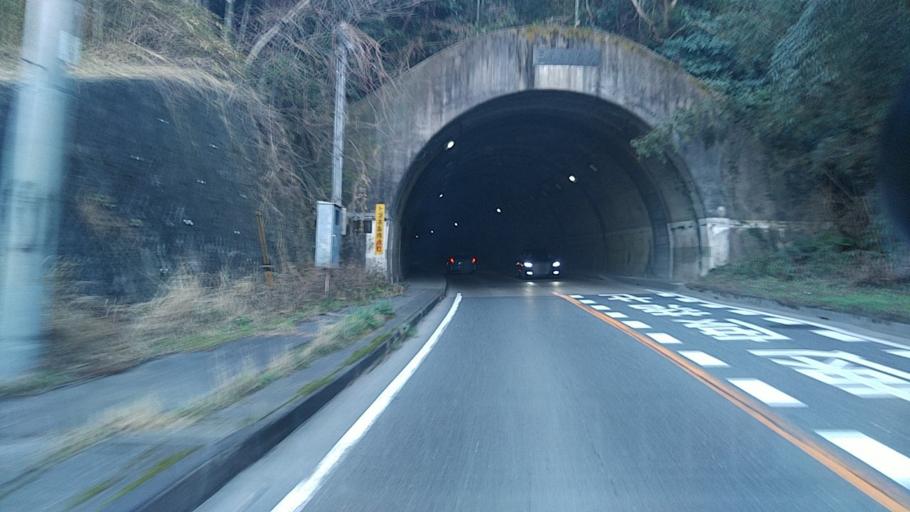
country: JP
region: Chiba
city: Kimitsu
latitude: 35.3160
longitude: 139.9475
